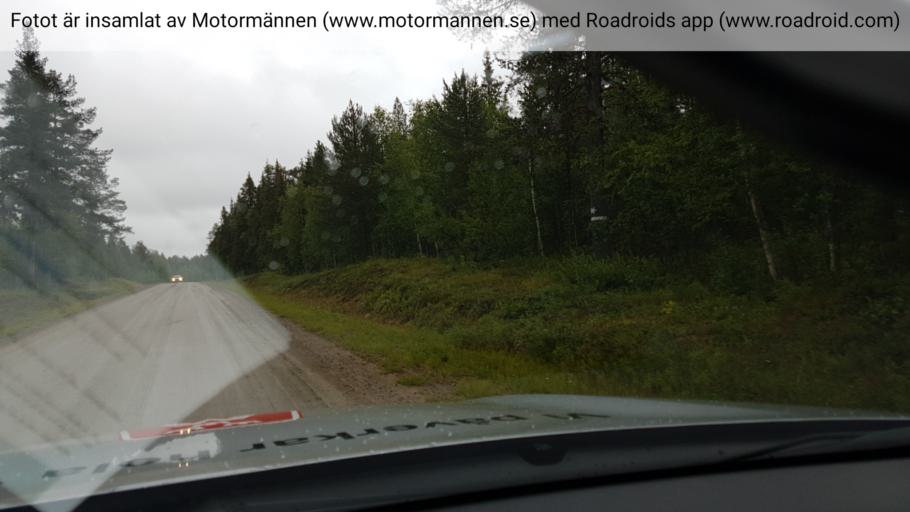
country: SE
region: Norrbotten
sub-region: Gallivare Kommun
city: Gaellivare
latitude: 66.7010
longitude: 20.4218
